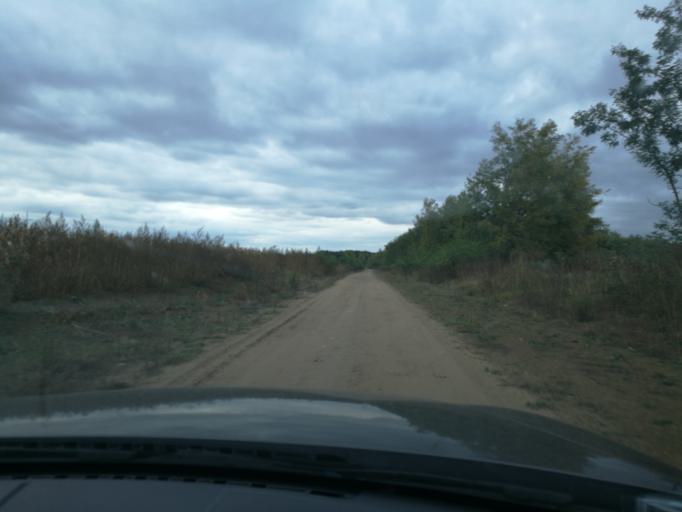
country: HU
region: Szabolcs-Szatmar-Bereg
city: Nyirpazony
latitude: 47.9907
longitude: 21.7885
